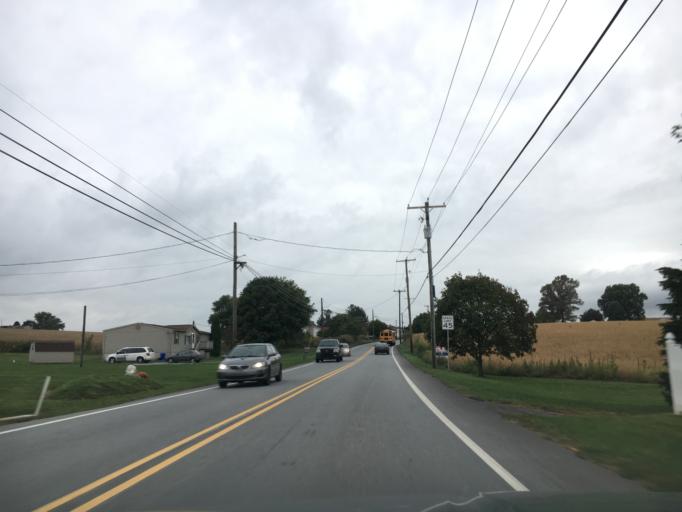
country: US
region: Pennsylvania
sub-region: York County
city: Windsor
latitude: 39.8817
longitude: -76.5368
